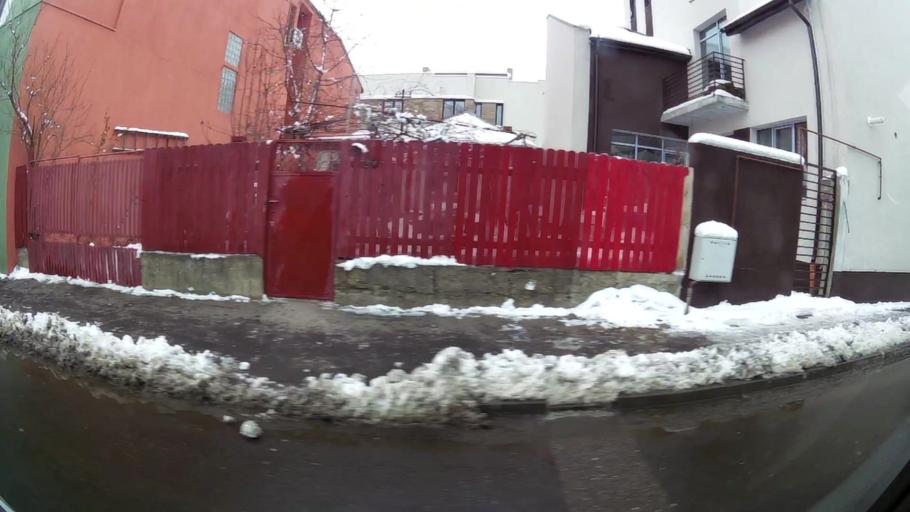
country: RO
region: Bucuresti
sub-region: Municipiul Bucuresti
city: Bucuresti
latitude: 44.3880
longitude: 26.0966
